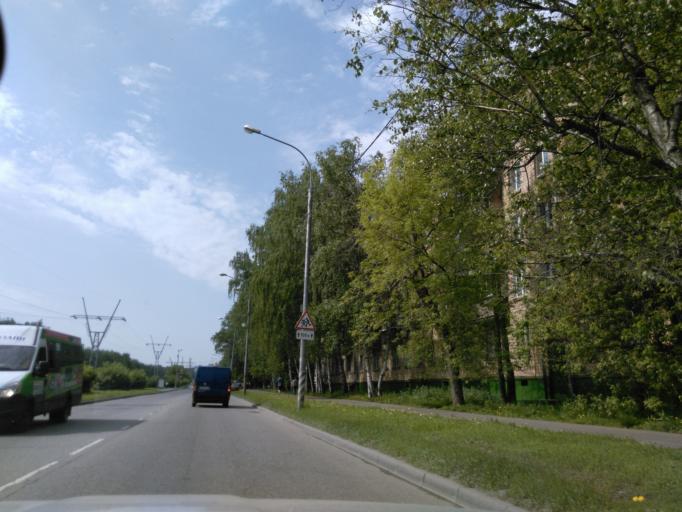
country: RU
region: Moscow
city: Golovinskiy
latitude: 55.8499
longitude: 37.5081
